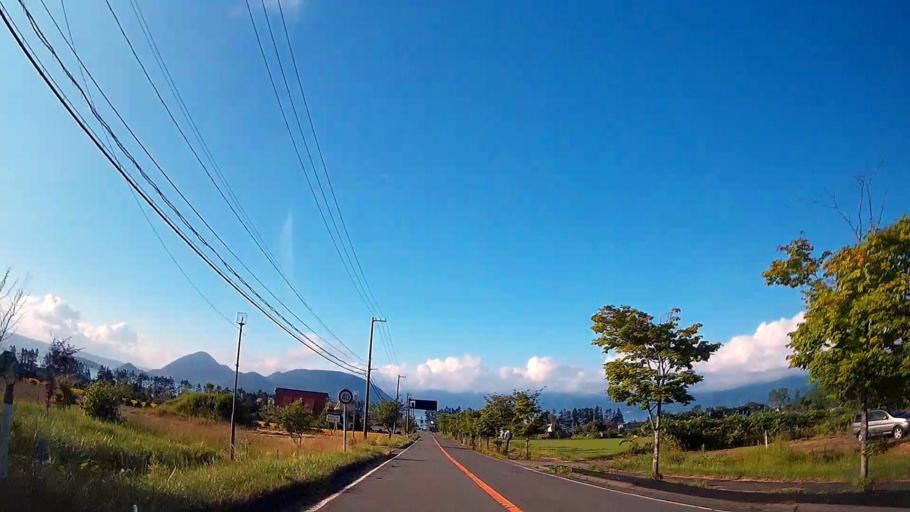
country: JP
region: Hokkaido
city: Date
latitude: 42.5539
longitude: 140.8623
